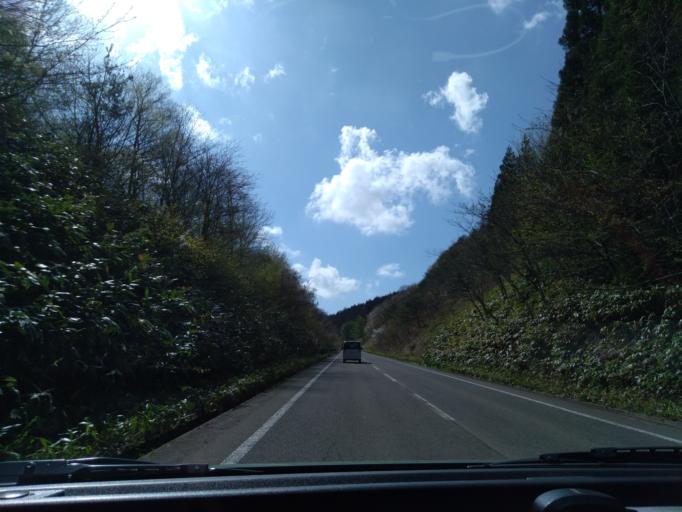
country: JP
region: Akita
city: Akita
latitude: 39.6962
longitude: 140.2592
